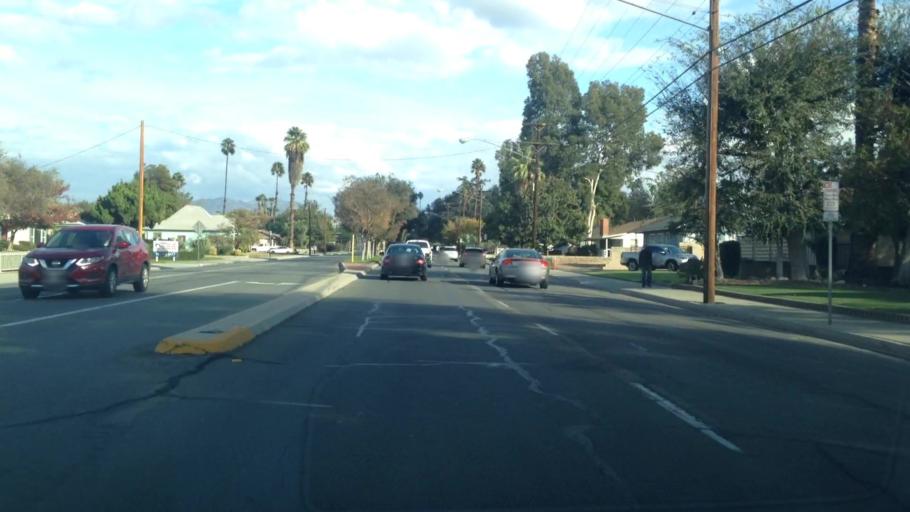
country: US
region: California
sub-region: Riverside County
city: Riverside
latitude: 33.9461
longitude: -117.4094
